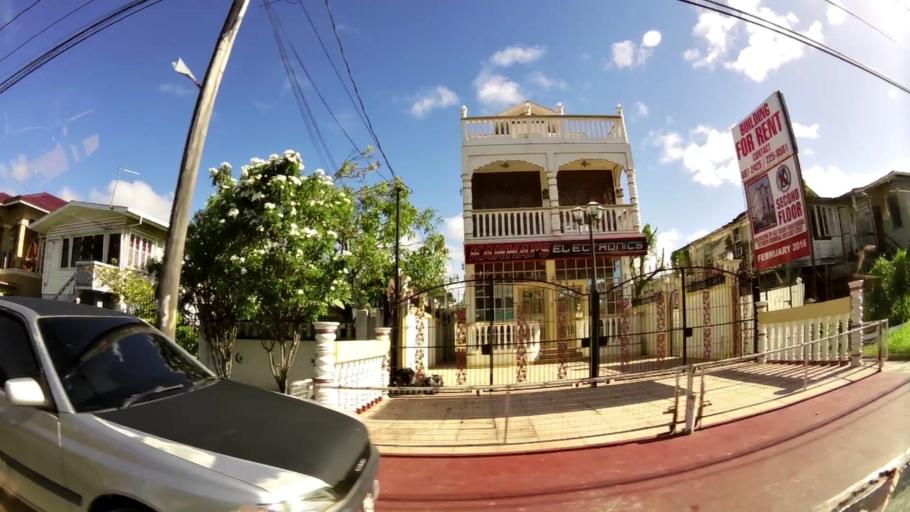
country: GY
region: Demerara-Mahaica
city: Georgetown
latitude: 6.8139
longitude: -58.1438
